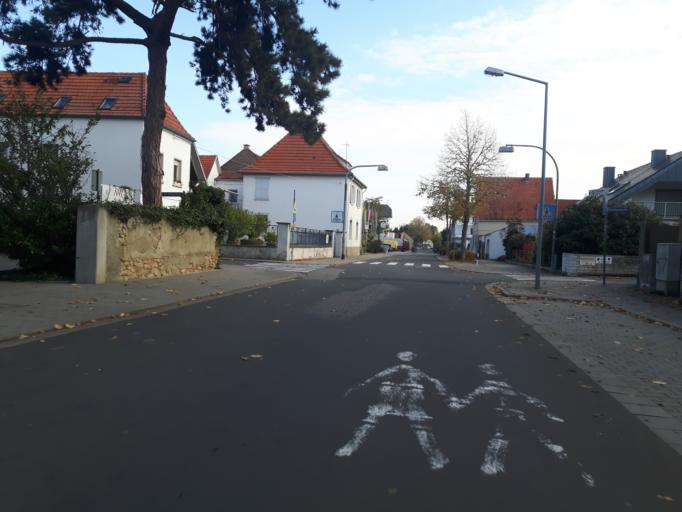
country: DE
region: Rheinland-Pfalz
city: Westhofen
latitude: 49.7041
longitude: 8.2521
